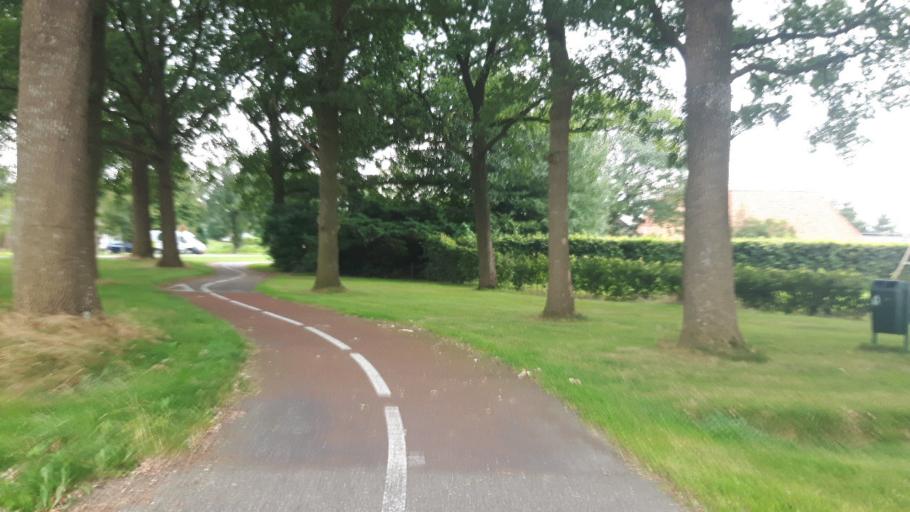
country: NL
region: Friesland
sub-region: Gemeente Weststellingwerf
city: Noordwolde
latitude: 52.9579
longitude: 6.2204
